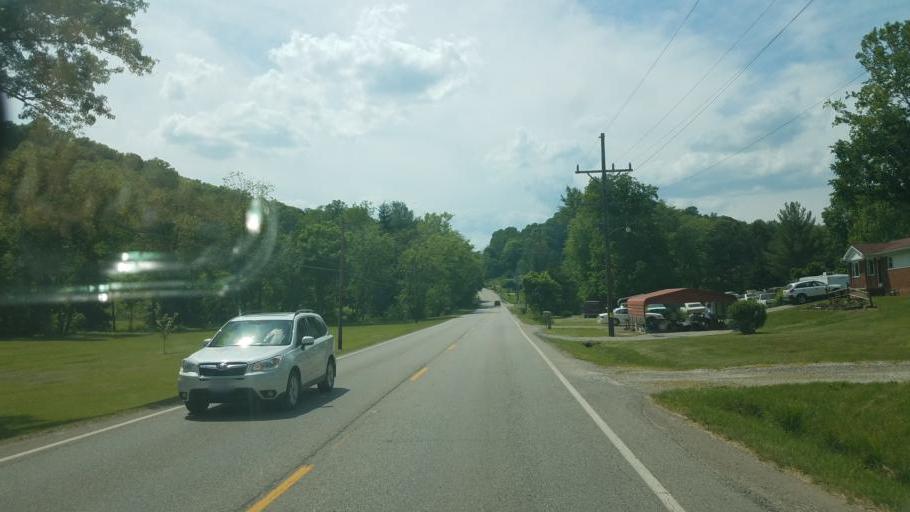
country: US
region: Ohio
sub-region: Meigs County
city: Middleport
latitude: 39.0286
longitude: -82.0939
